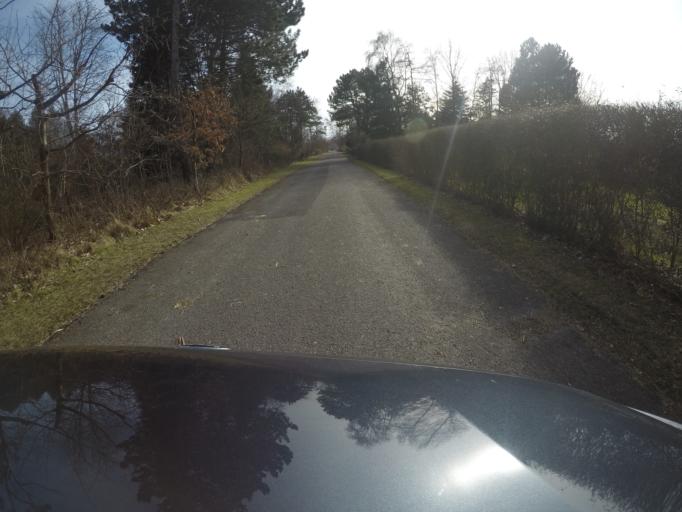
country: DK
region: Capital Region
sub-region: Halsnaes Kommune
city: Liseleje
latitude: 55.9959
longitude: 11.9242
